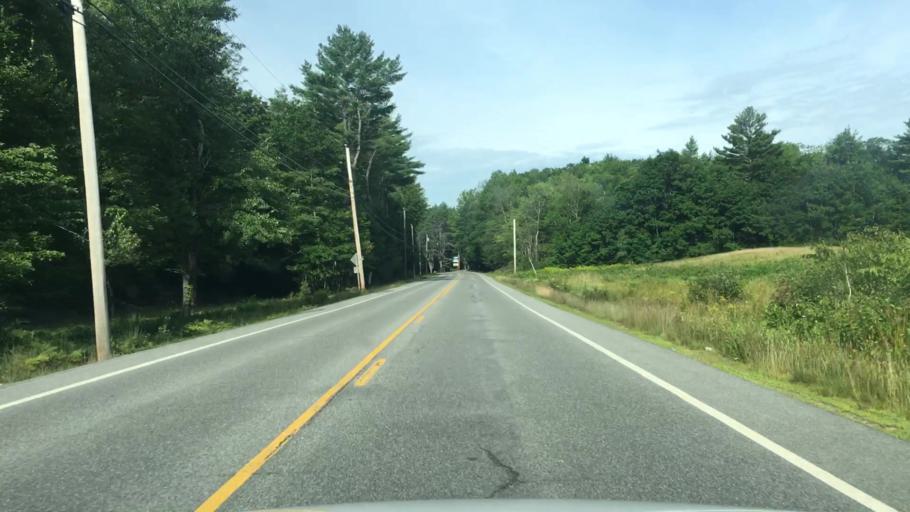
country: US
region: Maine
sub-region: Oxford County
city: Porter
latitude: 43.8025
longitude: -70.9063
